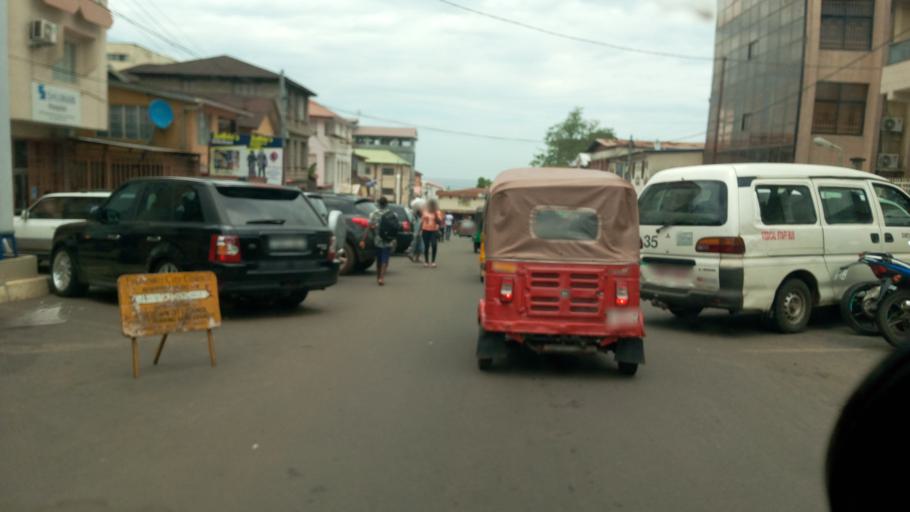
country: SL
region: Western Area
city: Freetown
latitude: 8.4873
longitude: -13.2366
